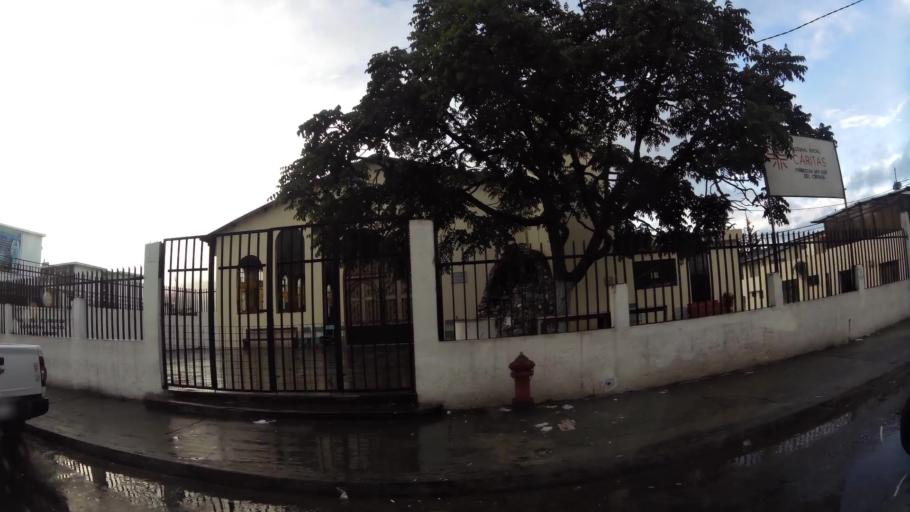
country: EC
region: Pichincha
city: Quito
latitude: -0.1066
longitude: -78.4933
